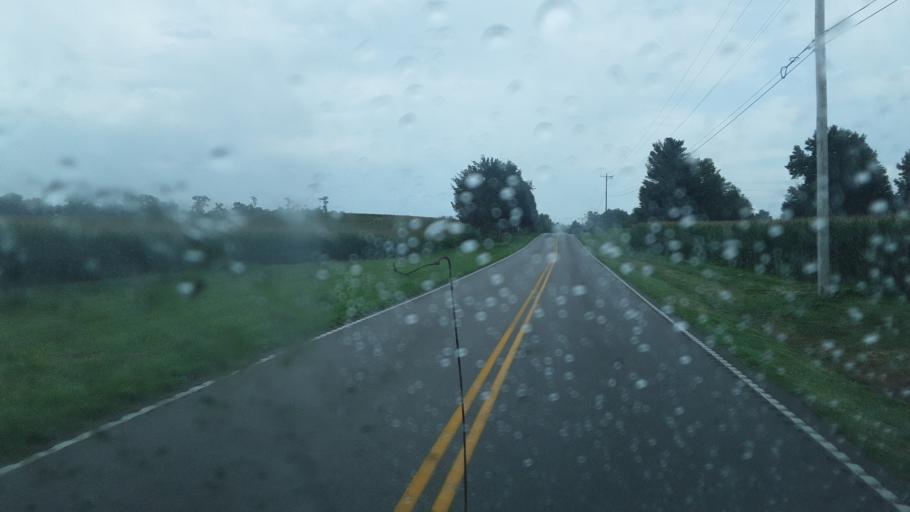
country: US
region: Kentucky
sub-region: Todd County
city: Guthrie
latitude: 36.6531
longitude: -87.1999
